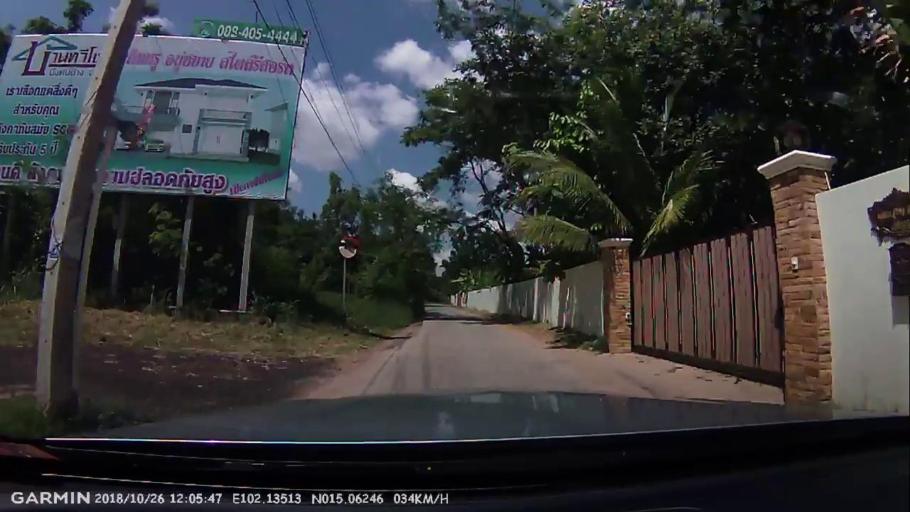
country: TH
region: Nakhon Ratchasima
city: Nakhon Ratchasima
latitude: 15.0625
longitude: 102.1351
